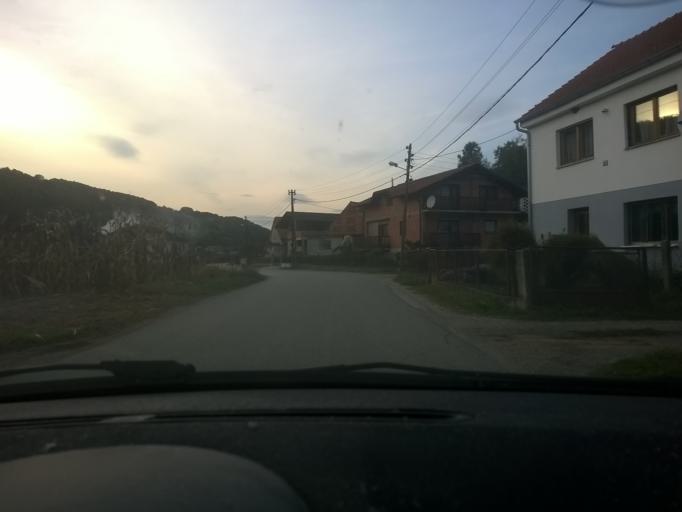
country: HR
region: Krapinsko-Zagorska
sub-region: Grad Krapina
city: Krapina
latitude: 46.0968
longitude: 15.8787
